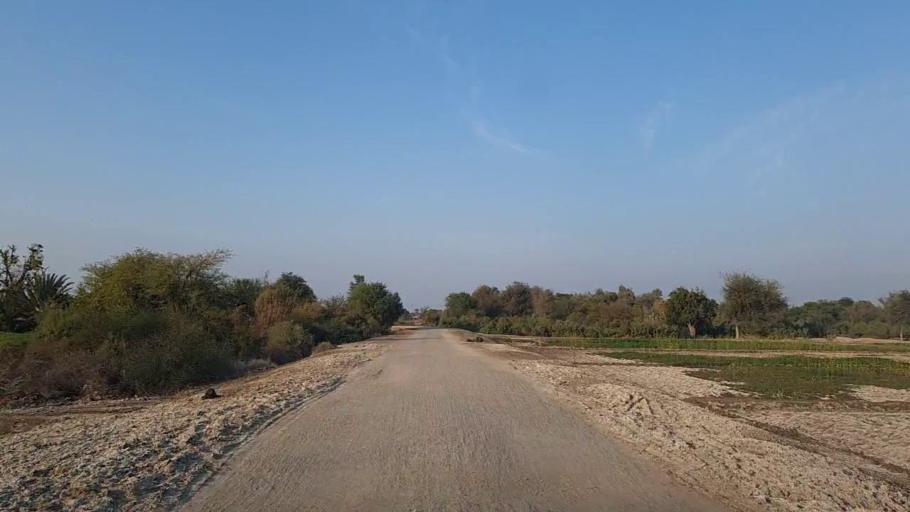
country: PK
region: Sindh
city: Jam Sahib
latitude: 26.3933
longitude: 68.5431
